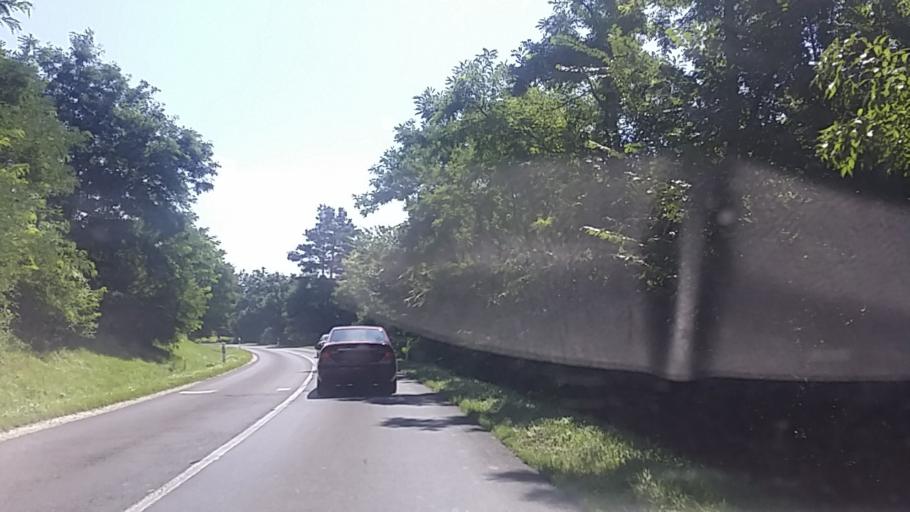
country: HU
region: Zala
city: Keszthely
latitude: 46.7038
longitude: 17.2396
